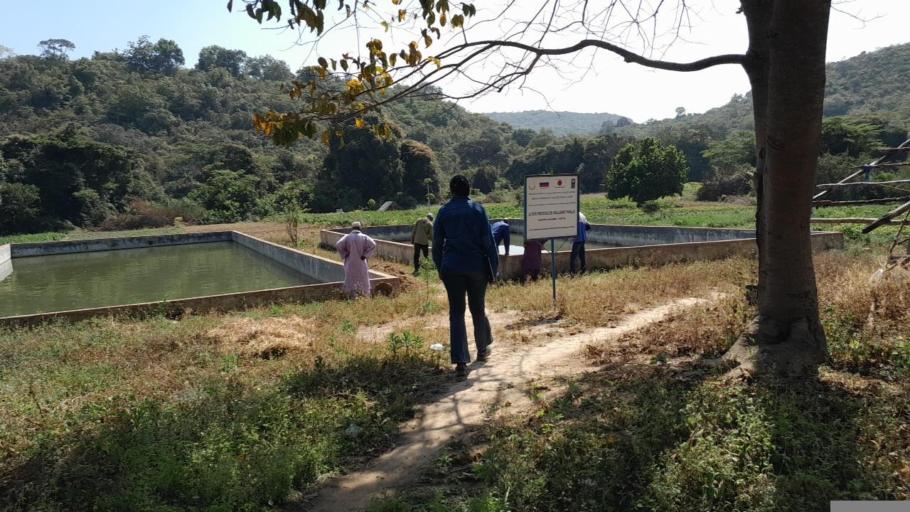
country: GN
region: Mamou
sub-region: Pita
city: Pita
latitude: 11.0722
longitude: -12.3695
